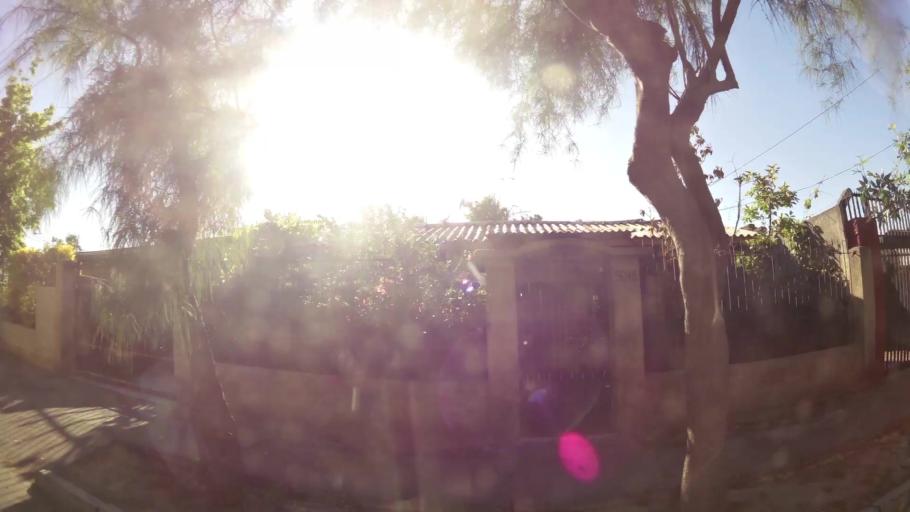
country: CL
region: Santiago Metropolitan
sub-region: Provincia de Maipo
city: San Bernardo
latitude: -33.5454
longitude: -70.6764
